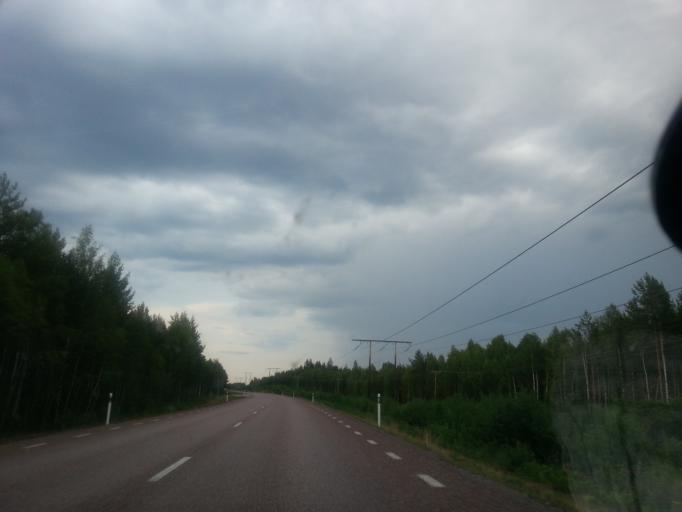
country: SE
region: Gaevleborg
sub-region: Hofors Kommun
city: Hofors
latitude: 60.5237
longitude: 16.4501
